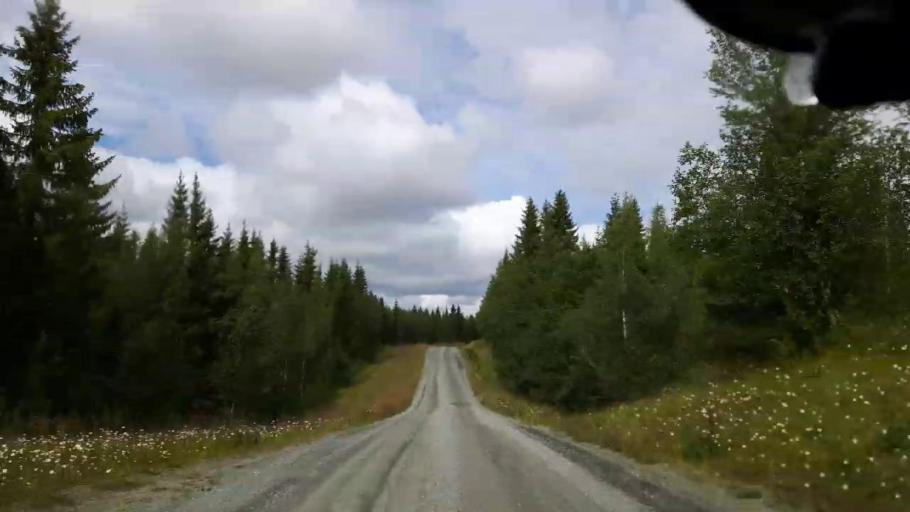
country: SE
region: Jaemtland
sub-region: Krokoms Kommun
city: Valla
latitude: 63.5588
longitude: 13.9165
